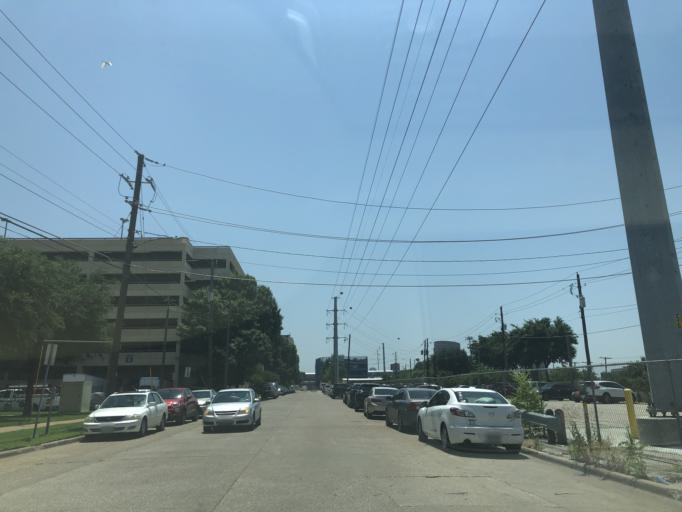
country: US
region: Texas
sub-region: Dallas County
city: Dallas
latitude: 32.8102
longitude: -96.8417
